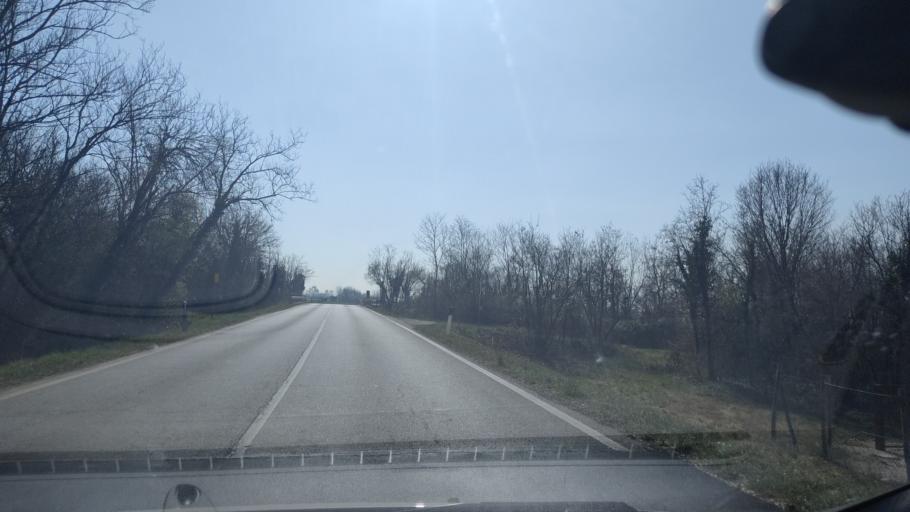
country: IT
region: Friuli Venezia Giulia
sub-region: Provincia di Pordenone
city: Budoia
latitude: 46.0312
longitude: 12.5533
